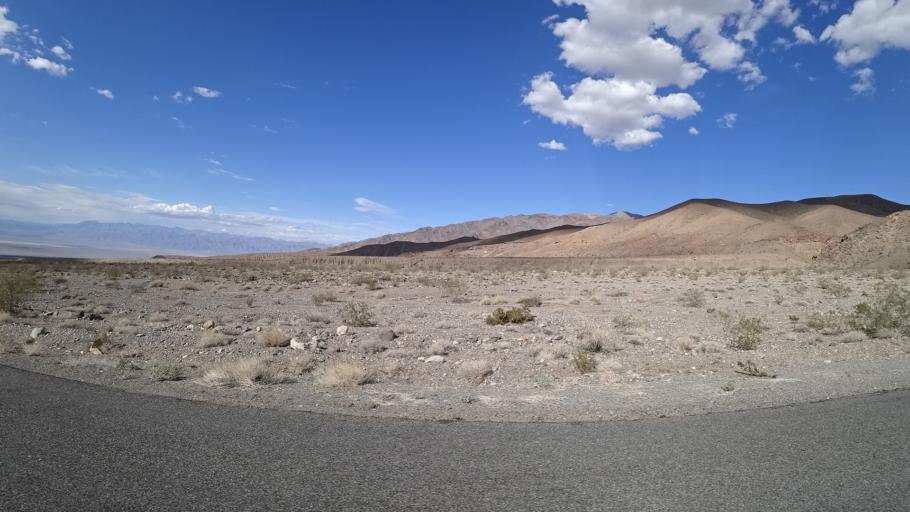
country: US
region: Nevada
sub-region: Nye County
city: Beatty
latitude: 36.4790
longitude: -117.2171
